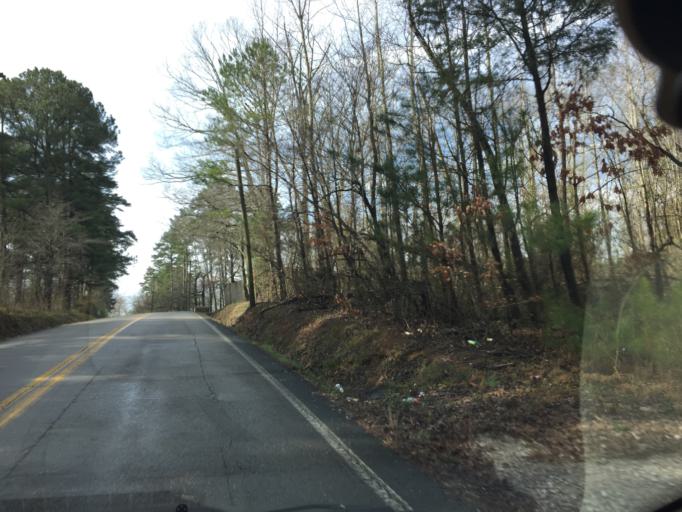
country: US
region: Tennessee
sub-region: Hamilton County
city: Collegedale
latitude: 35.0512
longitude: -85.1022
